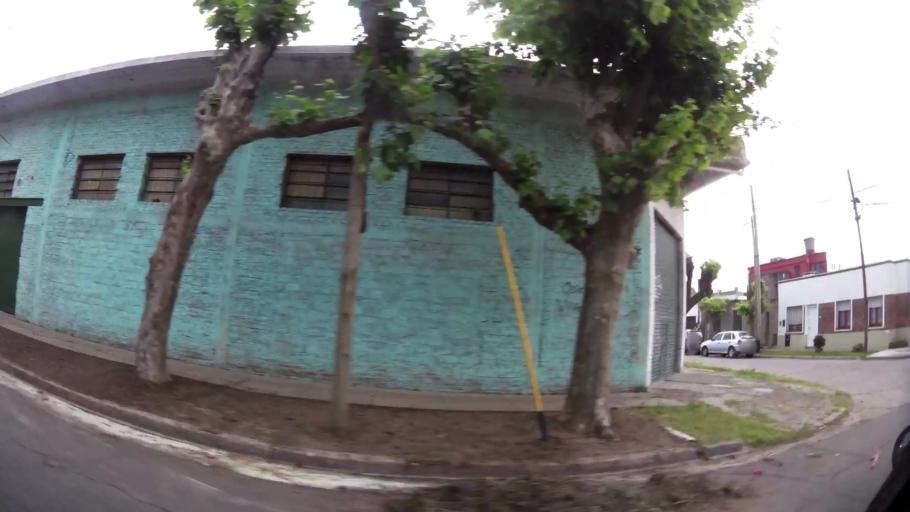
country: AR
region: Buenos Aires
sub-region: Partido de Quilmes
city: Quilmes
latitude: -34.7343
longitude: -58.2479
